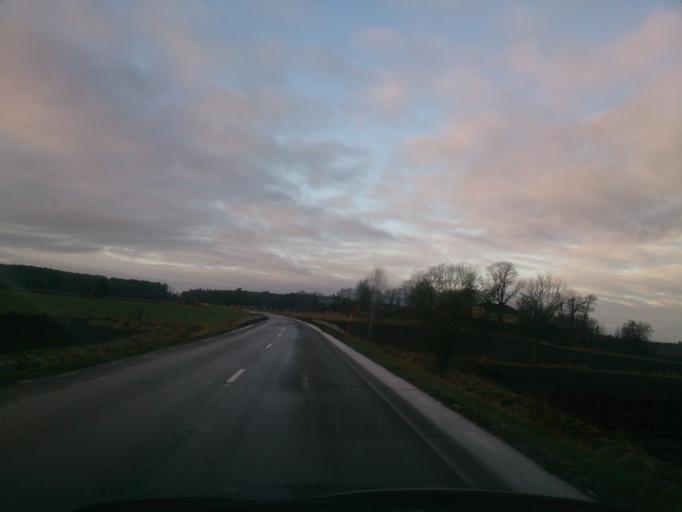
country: SE
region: OEstergoetland
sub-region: Linkopings Kommun
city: Linghem
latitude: 58.4128
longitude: 15.9097
